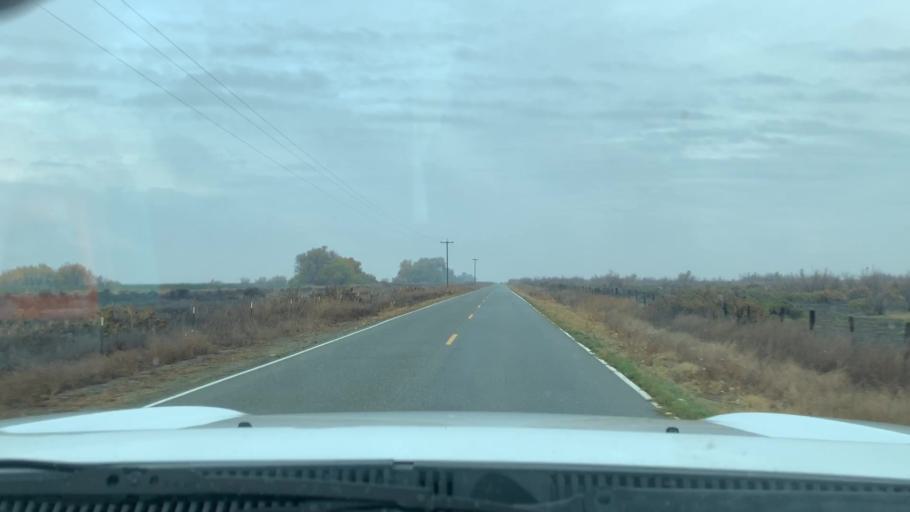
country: US
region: California
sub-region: Kern County
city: Lost Hills
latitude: 35.7219
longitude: -119.5795
